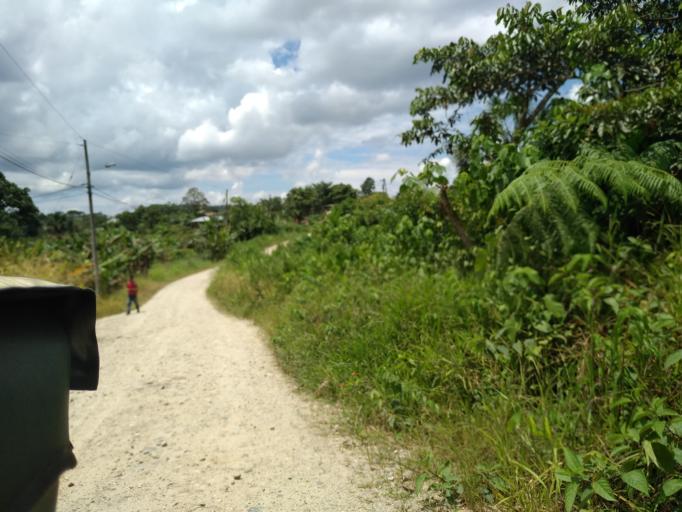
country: EC
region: Napo
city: Tena
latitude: -0.9920
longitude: -77.8250
